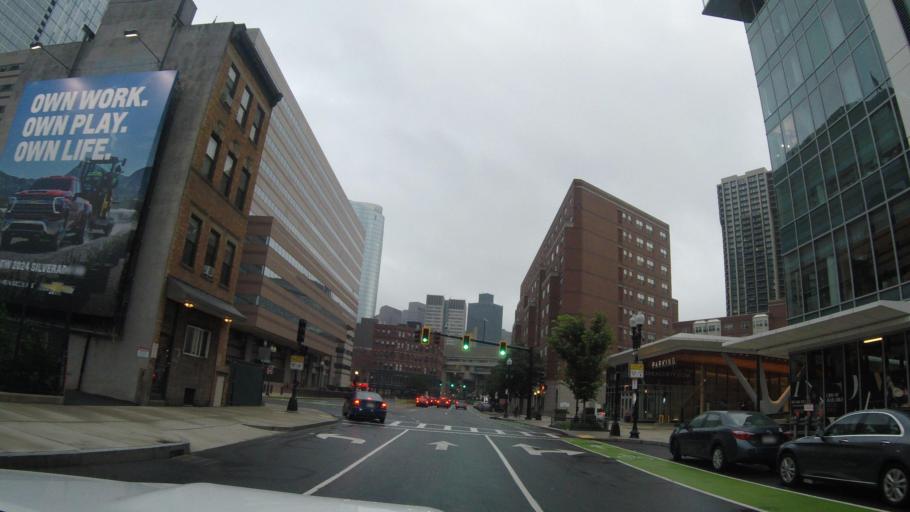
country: US
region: Massachusetts
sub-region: Suffolk County
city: Boston
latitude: 42.3657
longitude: -71.0646
